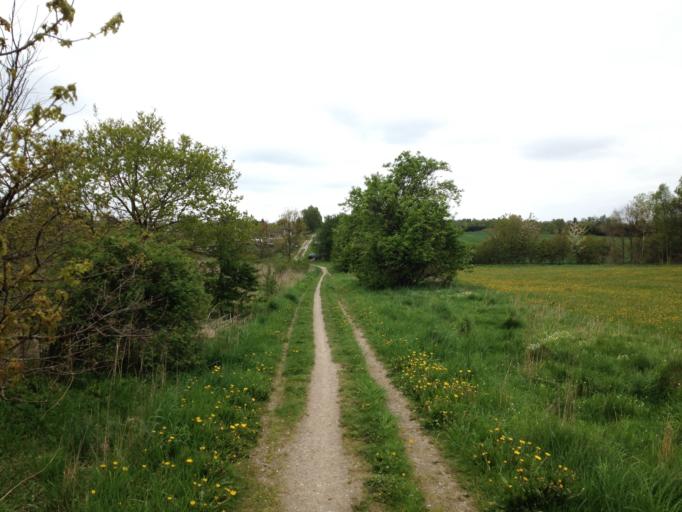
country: DK
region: Capital Region
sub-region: Fredensborg Kommune
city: Niva
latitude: 55.9490
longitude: 12.5040
